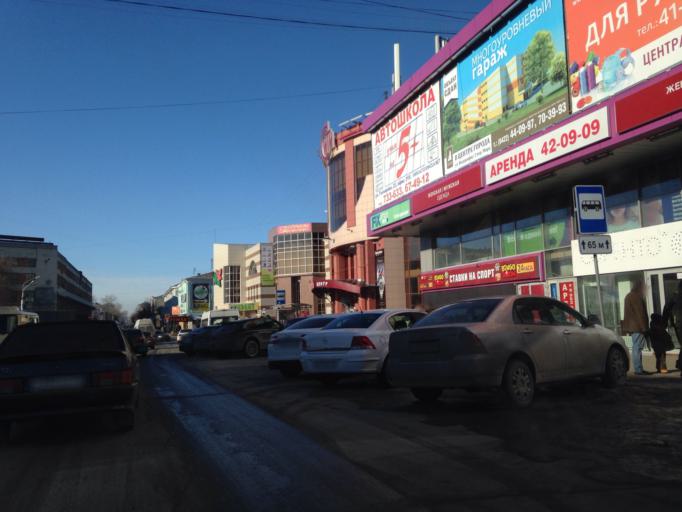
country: RU
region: Ulyanovsk
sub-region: Ulyanovskiy Rayon
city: Ulyanovsk
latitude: 54.3190
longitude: 48.3971
